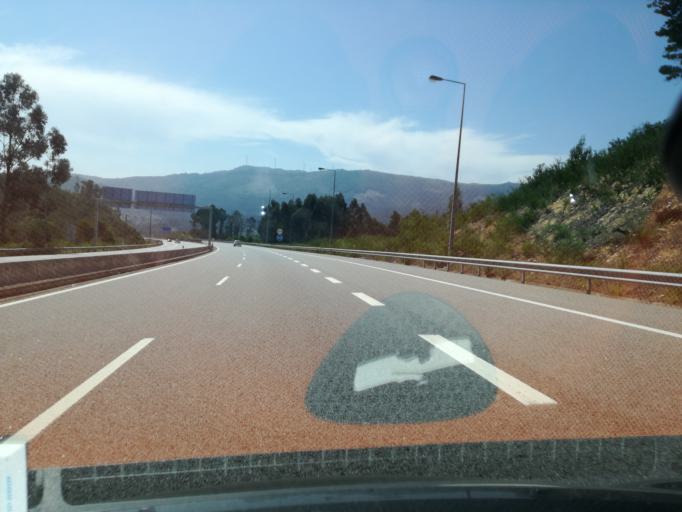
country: PT
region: Viana do Castelo
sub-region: Caminha
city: Vila Praia de Ancora
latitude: 41.8128
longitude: -8.8054
